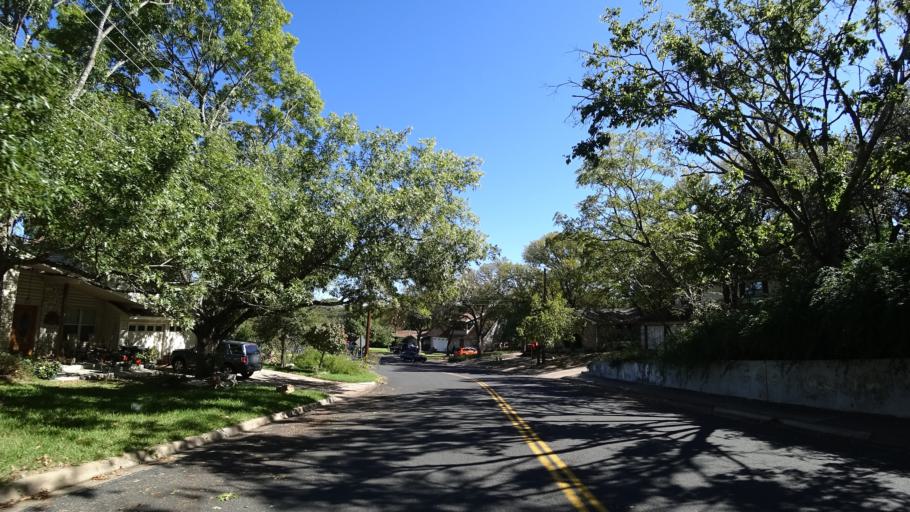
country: US
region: Texas
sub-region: Travis County
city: Rollingwood
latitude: 30.2223
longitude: -97.7994
